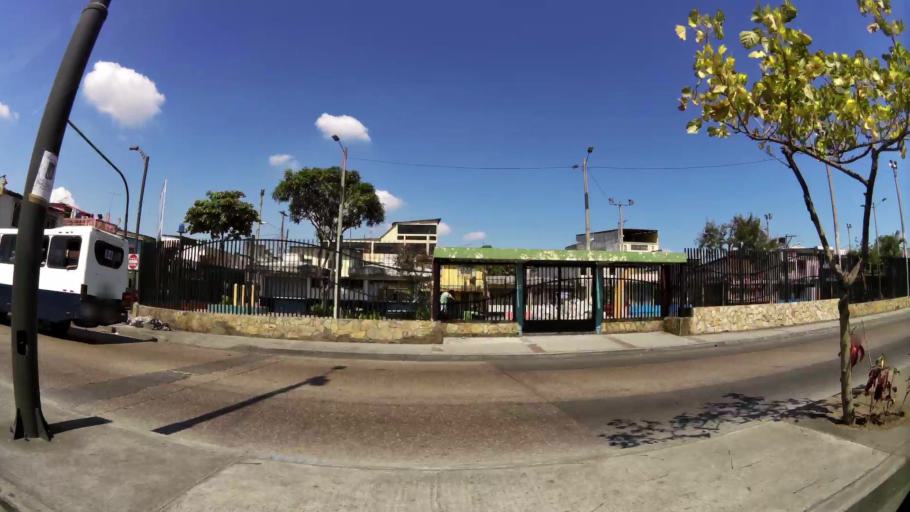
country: EC
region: Guayas
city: Guayaquil
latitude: -2.2088
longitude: -79.9283
